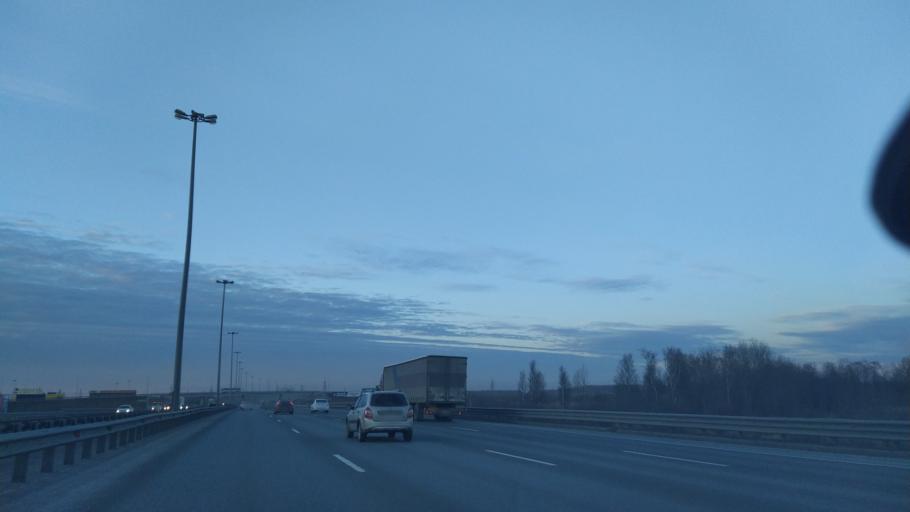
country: RU
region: Leningrad
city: Rybatskoye
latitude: 59.9120
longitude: 30.5259
